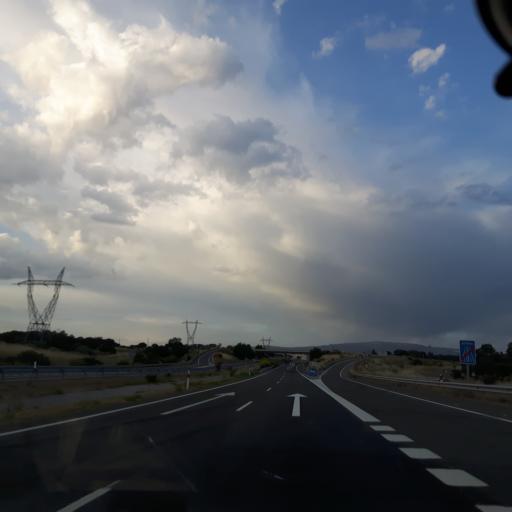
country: ES
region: Castille and Leon
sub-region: Provincia de Salamanca
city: Fuentes de Bejar
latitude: 40.5019
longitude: -5.6761
